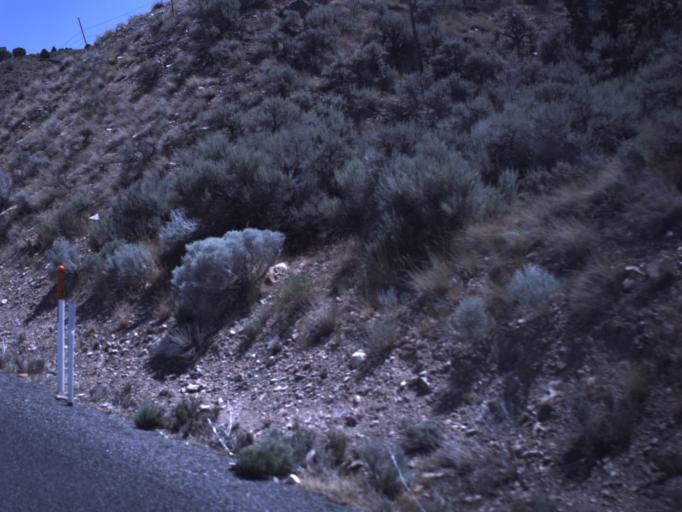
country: US
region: Utah
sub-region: Juab County
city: Nephi
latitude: 39.5565
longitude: -112.2117
